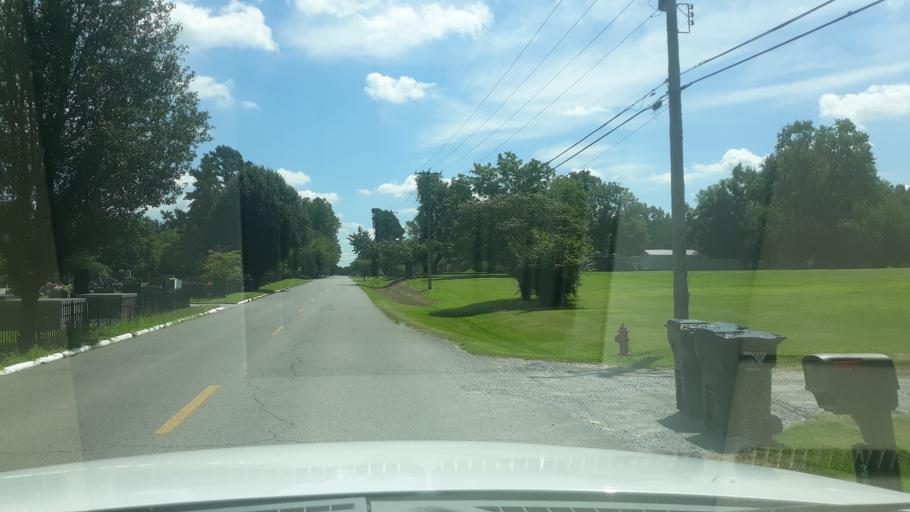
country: US
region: Illinois
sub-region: Saline County
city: Harrisburg
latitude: 37.7278
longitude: -88.5610
